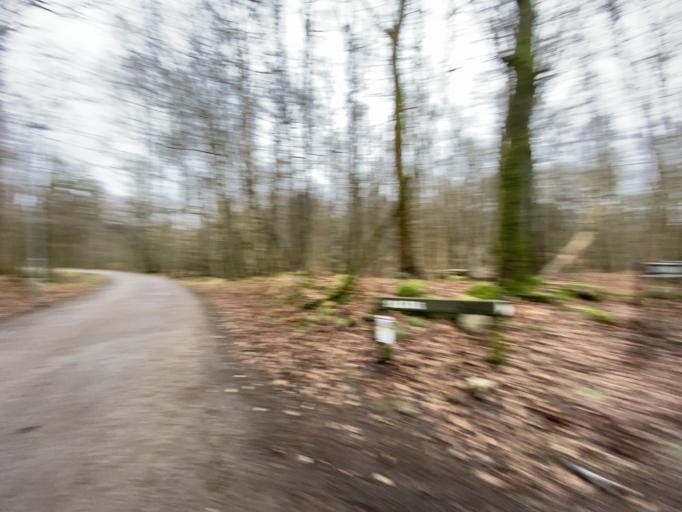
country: SE
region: Vaestra Goetaland
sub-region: Molndal
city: Moelndal
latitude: 57.7068
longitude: 12.0310
